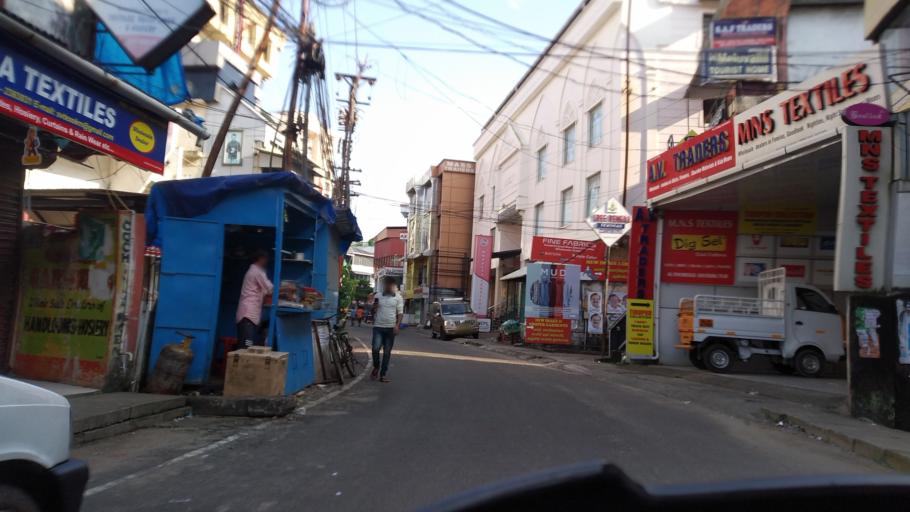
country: IN
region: Kerala
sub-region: Ernakulam
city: Cochin
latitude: 9.9789
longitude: 76.2788
